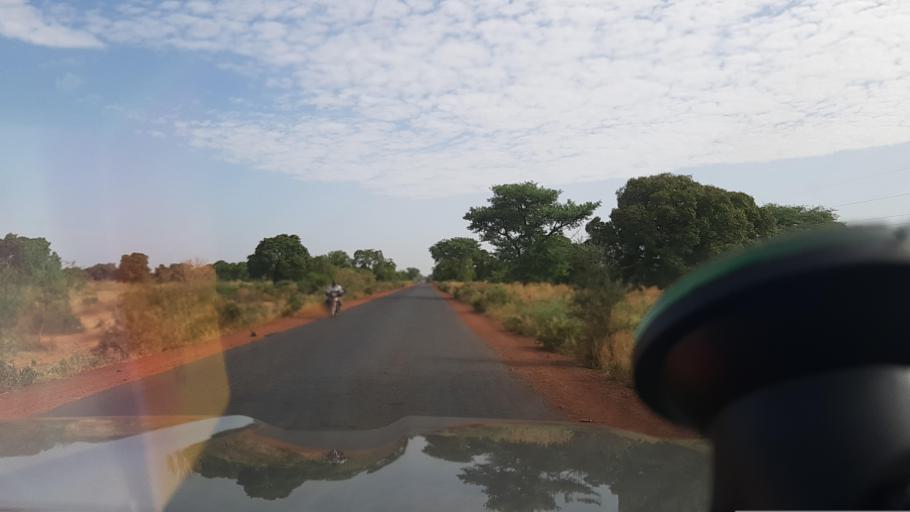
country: ML
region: Segou
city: Segou
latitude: 13.5186
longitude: -6.1366
